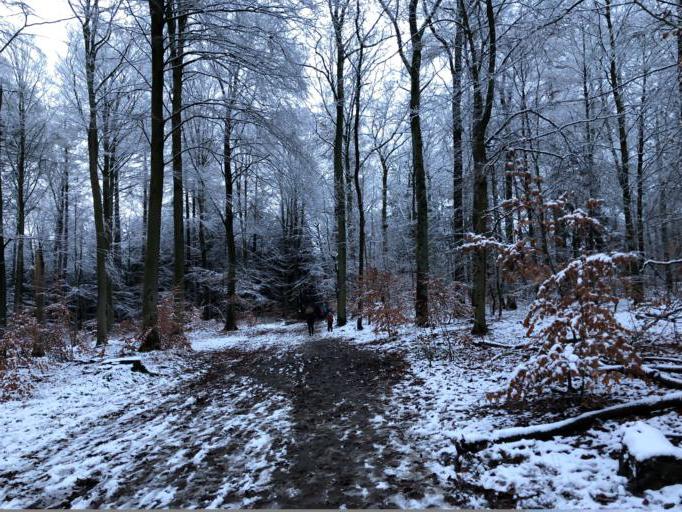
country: DK
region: Capital Region
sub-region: Rudersdal Kommune
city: Holte
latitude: 55.8072
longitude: 12.4791
